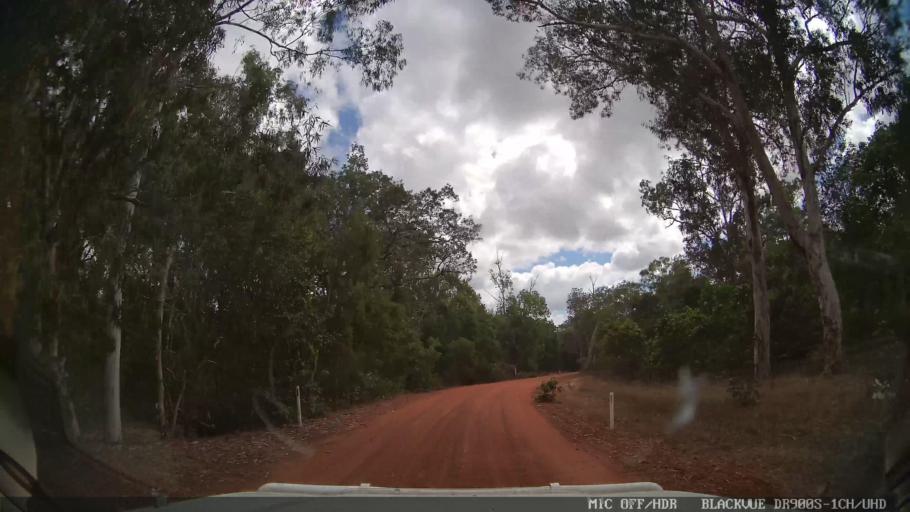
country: AU
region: Queensland
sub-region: Cook
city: Cooktown
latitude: -15.3038
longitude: 144.6159
